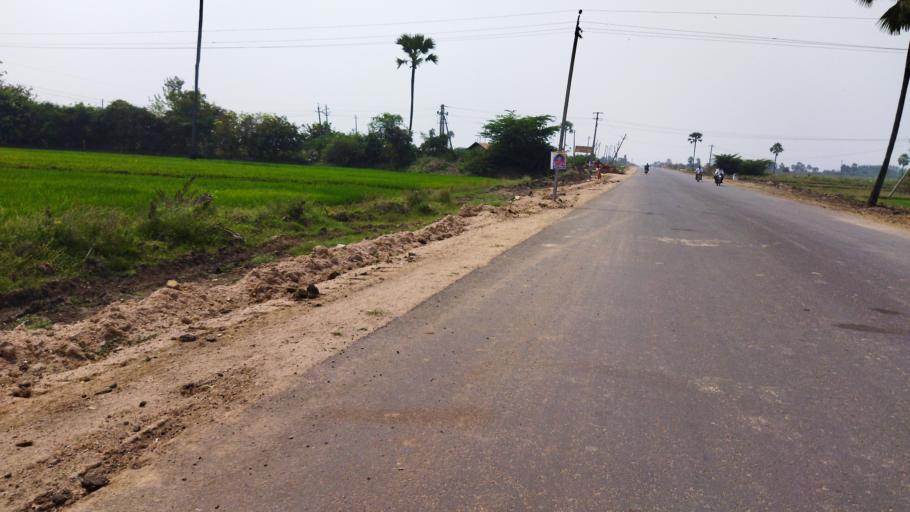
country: IN
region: Telangana
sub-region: Nalgonda
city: Nalgonda
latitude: 17.1499
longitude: 79.4030
